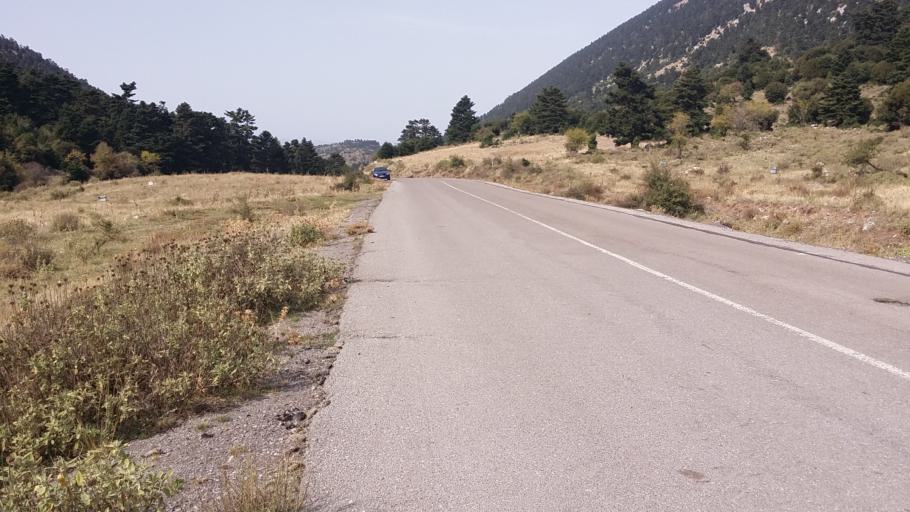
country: GR
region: Central Greece
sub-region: Nomos Voiotias
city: Kyriaki
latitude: 38.3357
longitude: 22.8318
